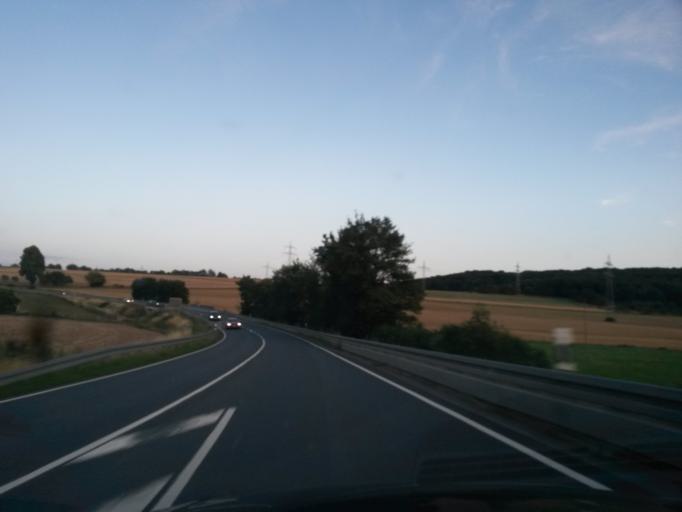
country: DE
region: Bavaria
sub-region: Regierungsbezirk Unterfranken
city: Remlingen
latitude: 49.8011
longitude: 9.6903
